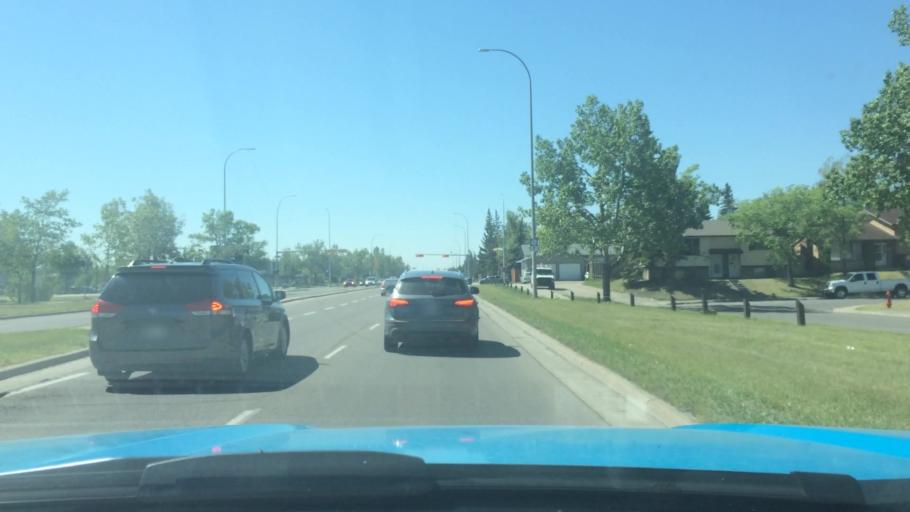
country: CA
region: Alberta
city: Calgary
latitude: 51.0777
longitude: -113.9585
